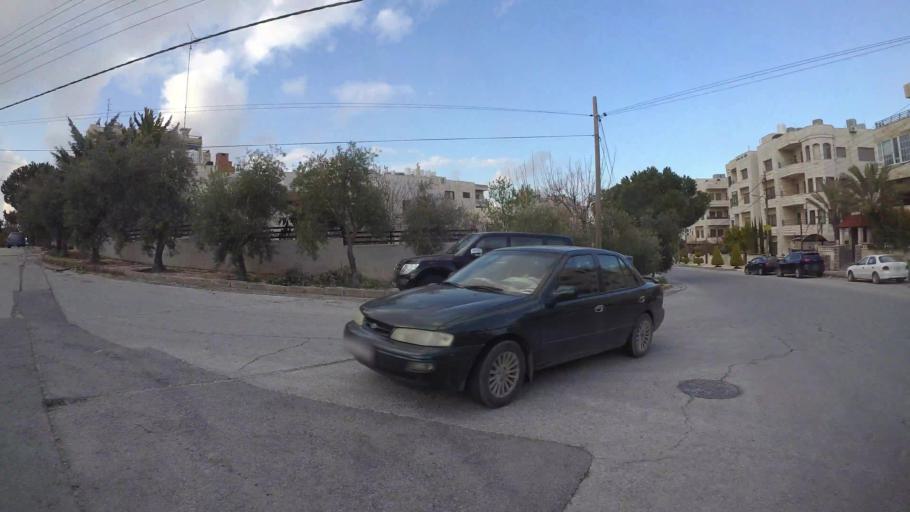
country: JO
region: Amman
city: Al Jubayhah
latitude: 31.9790
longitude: 35.8610
